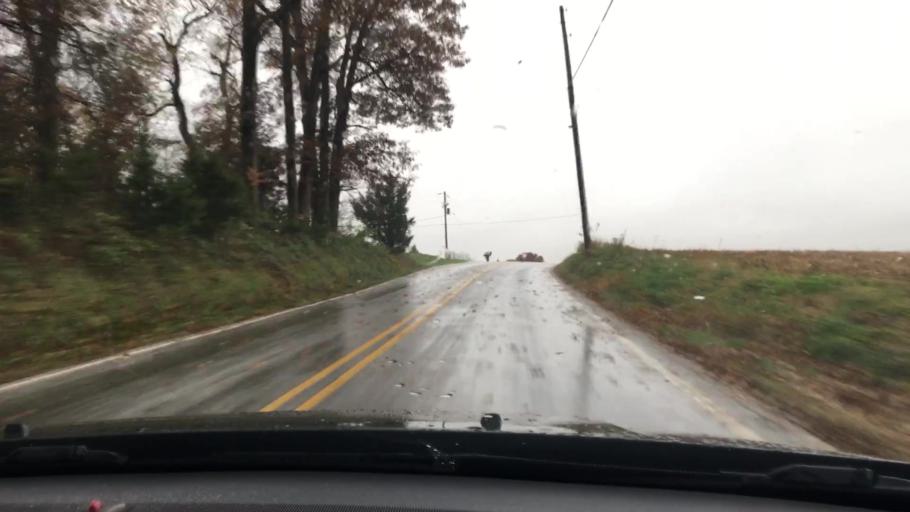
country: US
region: Pennsylvania
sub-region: York County
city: Susquehanna Trails
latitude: 39.7810
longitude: -76.4403
